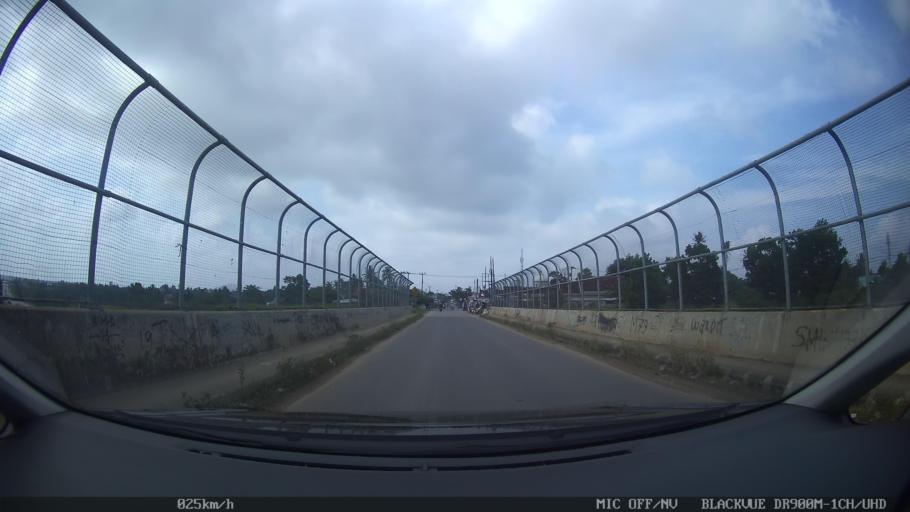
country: ID
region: Lampung
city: Kedaton
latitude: -5.3315
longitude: 105.2934
